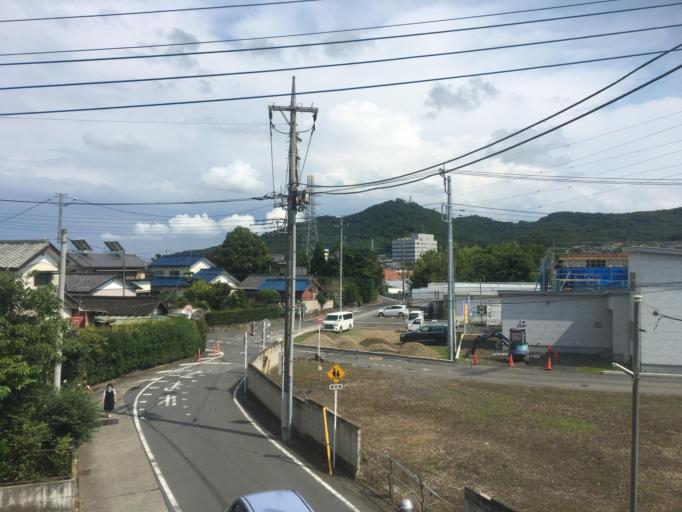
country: JP
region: Gunma
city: Kiryu
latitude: 36.3909
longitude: 139.3177
